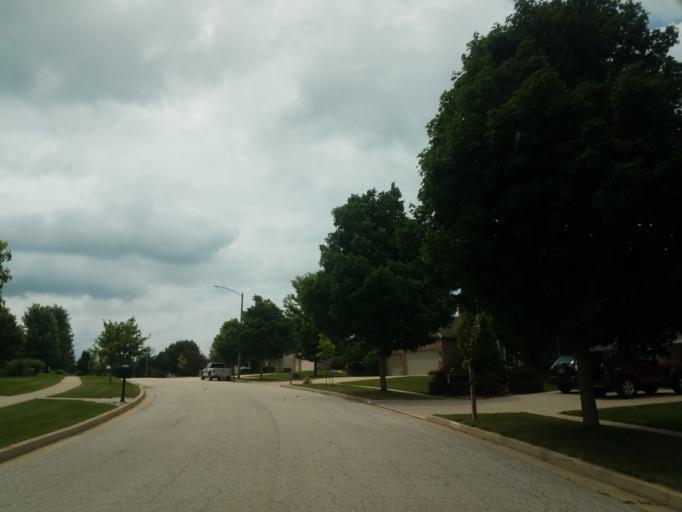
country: US
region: Illinois
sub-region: McLean County
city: Twin Grove
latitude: 40.4505
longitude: -89.0442
